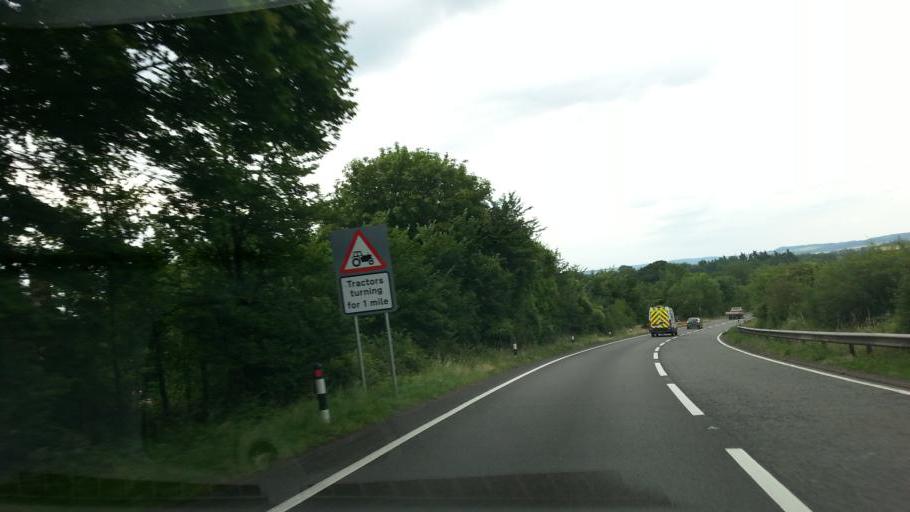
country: GB
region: England
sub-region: Herefordshire
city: Marstow
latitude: 51.8913
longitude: -2.6371
